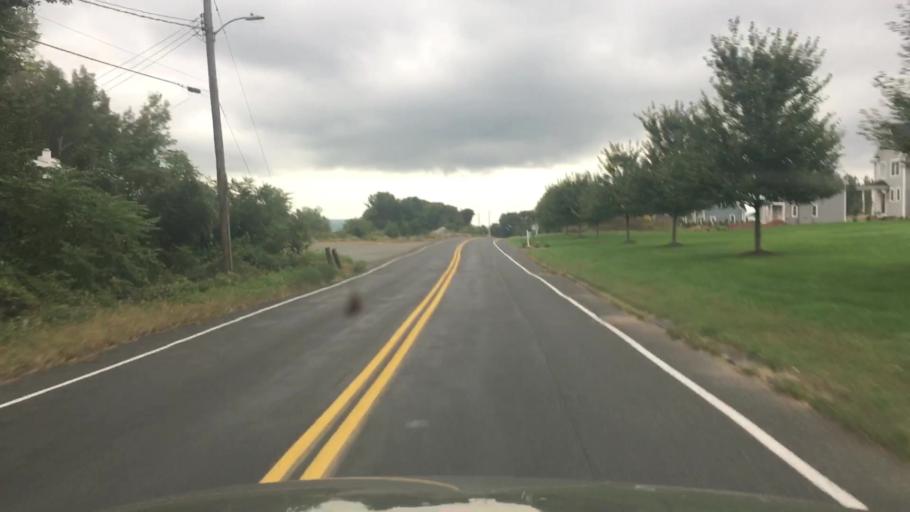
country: US
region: Connecticut
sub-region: Tolland County
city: Somers
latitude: 42.0076
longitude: -72.4807
